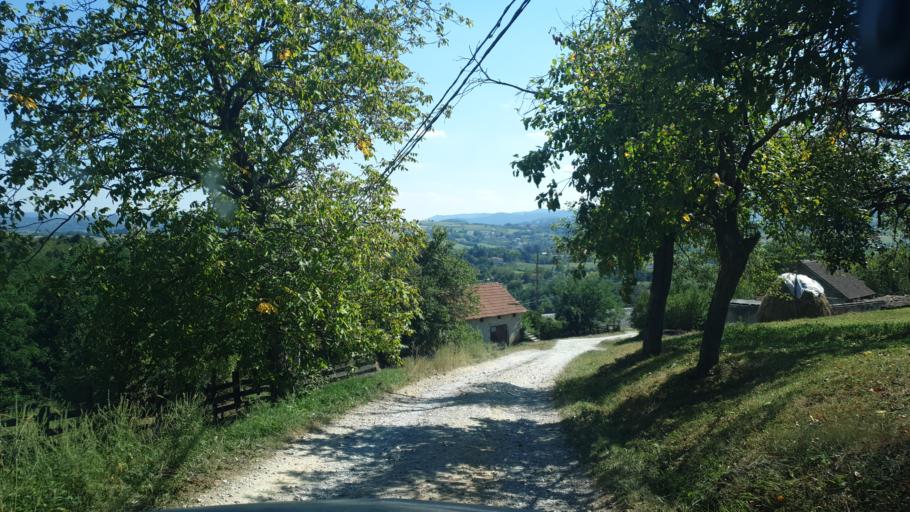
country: RS
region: Central Serbia
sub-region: Kolubarski Okrug
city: Mionica
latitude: 44.1985
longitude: 20.0221
